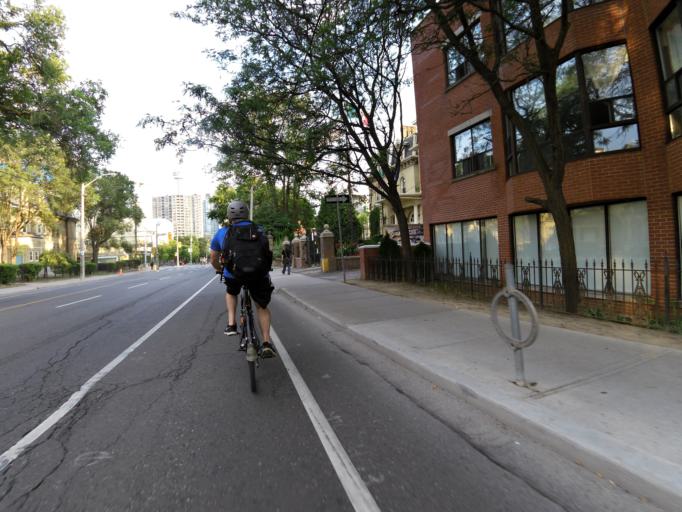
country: CA
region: Ontario
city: Toronto
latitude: 43.6544
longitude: -79.3942
